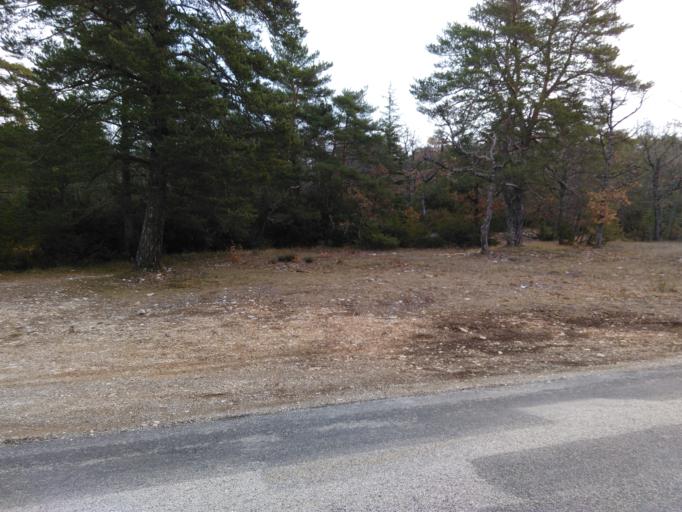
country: FR
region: Provence-Alpes-Cote d'Azur
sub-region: Departement du Vaucluse
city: Villes-sur-Auzon
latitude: 44.1012
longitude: 5.2799
